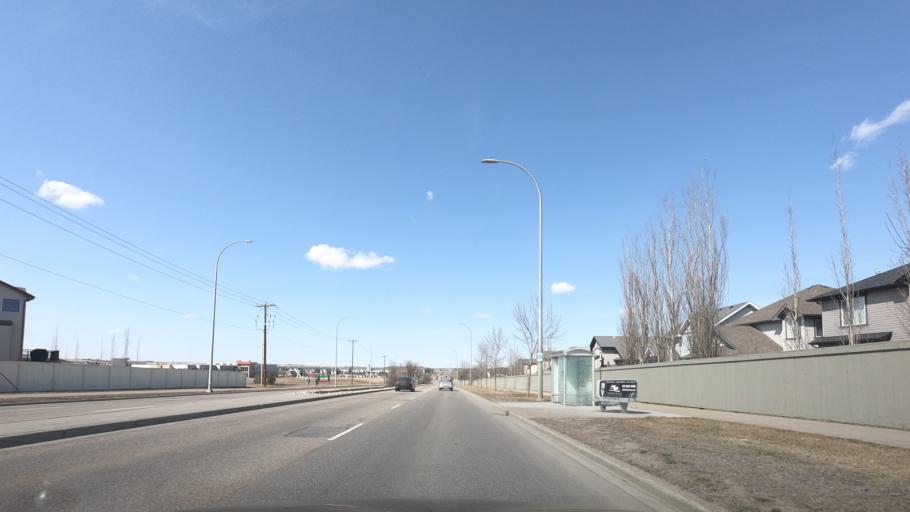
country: CA
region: Alberta
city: Airdrie
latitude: 51.2668
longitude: -114.0248
